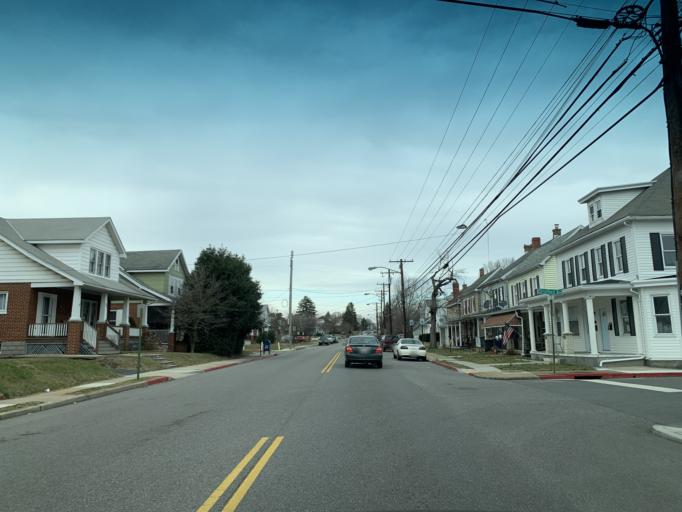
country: US
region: Maryland
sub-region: Washington County
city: Hagerstown
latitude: 39.6537
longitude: -77.7309
